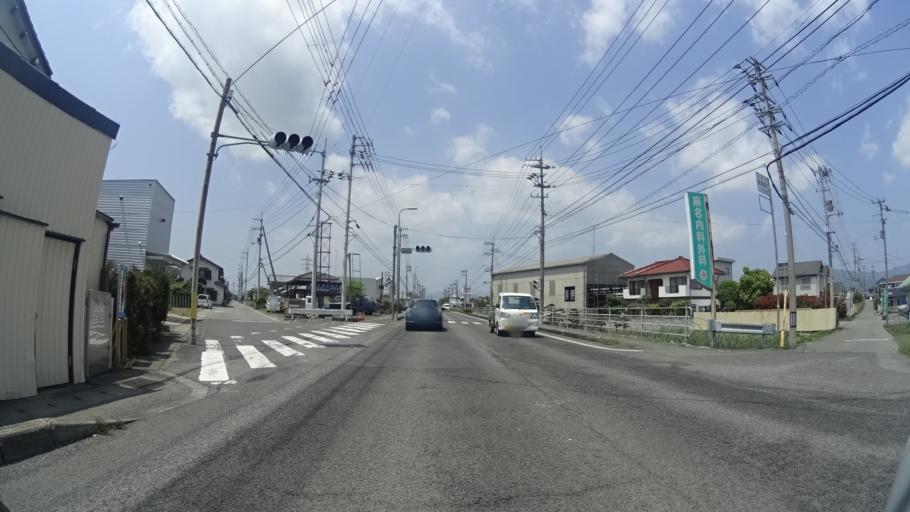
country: JP
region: Tokushima
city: Ishii
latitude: 34.0724
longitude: 134.3965
